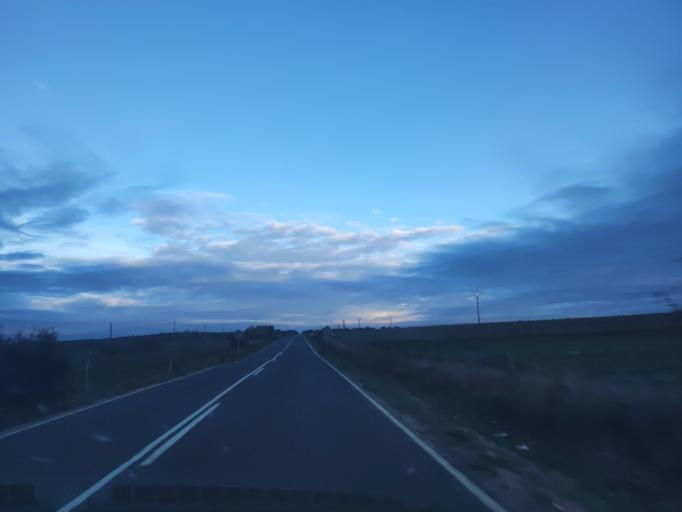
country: ES
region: Castille and Leon
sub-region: Provincia de Salamanca
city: Saelices el Chico
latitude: 40.6511
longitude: -6.5961
